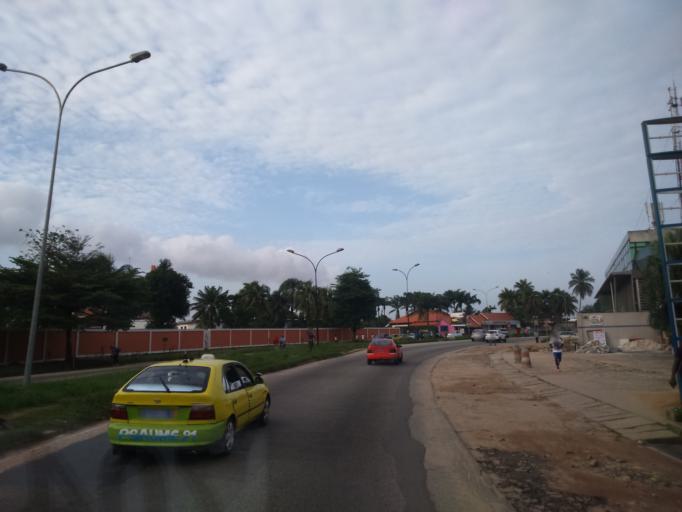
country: CI
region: Lagunes
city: Abidjan
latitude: 5.3616
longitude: -3.9976
